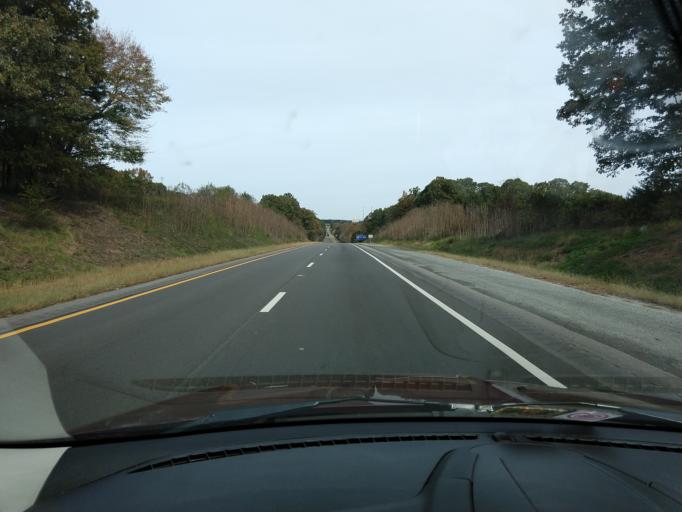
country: US
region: Virginia
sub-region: Pittsylvania County
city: Gretna
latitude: 36.9374
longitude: -79.3763
